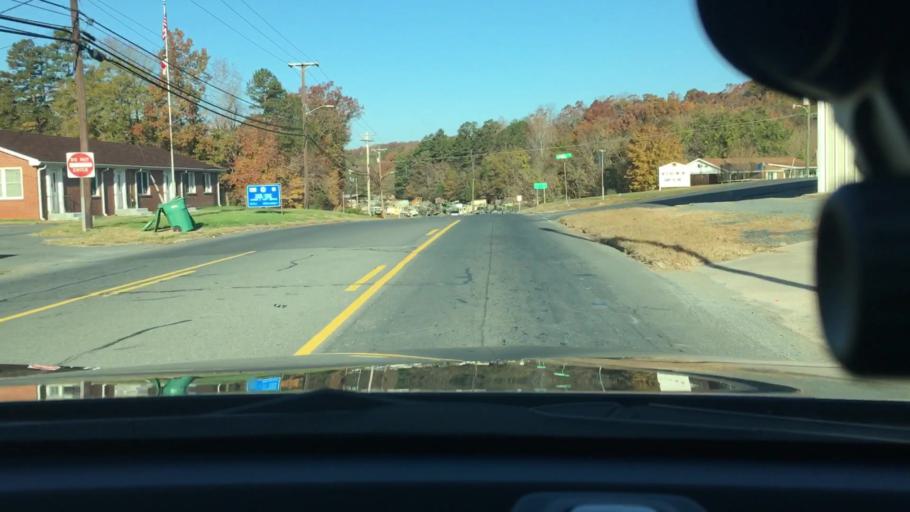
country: US
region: North Carolina
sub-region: Stanly County
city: Albemarle
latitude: 35.3553
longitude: -80.2161
